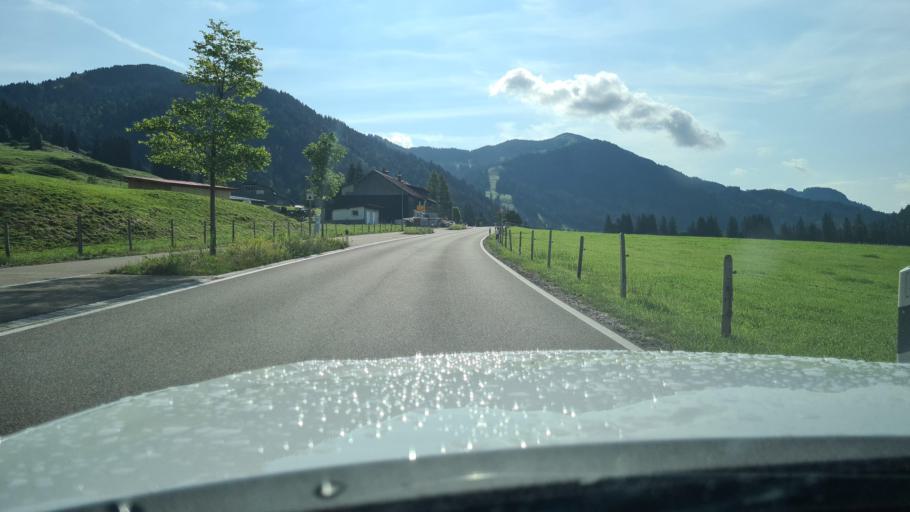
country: DE
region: Bavaria
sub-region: Swabia
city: Balderschwang
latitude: 47.4658
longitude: 10.1072
